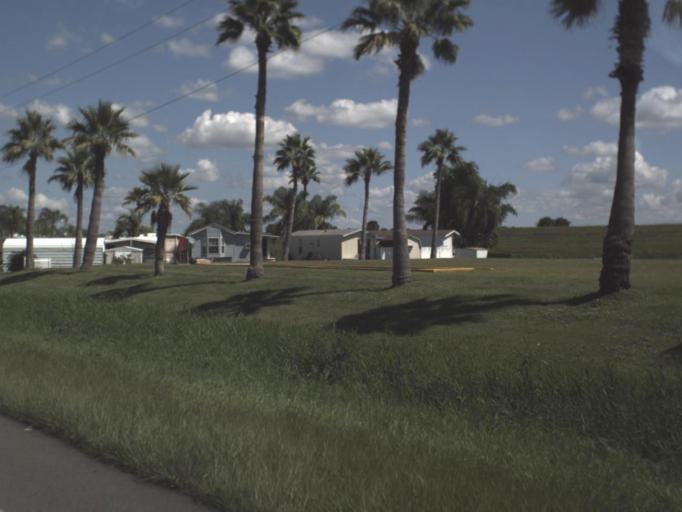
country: US
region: Florida
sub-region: Glades County
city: Buckhead Ridge
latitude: 27.1647
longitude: -80.8614
